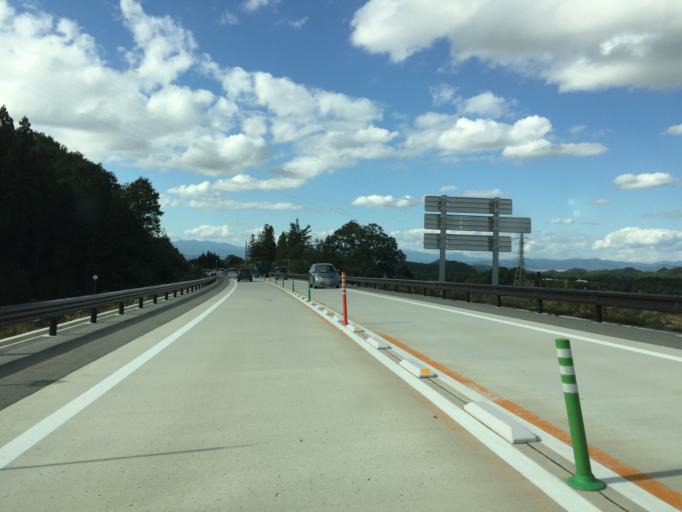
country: JP
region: Yamagata
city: Yonezawa
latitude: 37.8894
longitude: 140.1708
